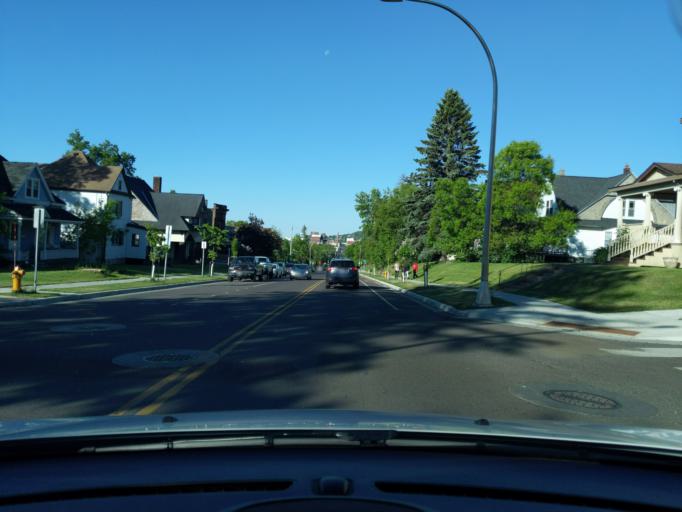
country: US
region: Minnesota
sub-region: Saint Louis County
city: Duluth
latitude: 46.8049
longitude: -92.0826
